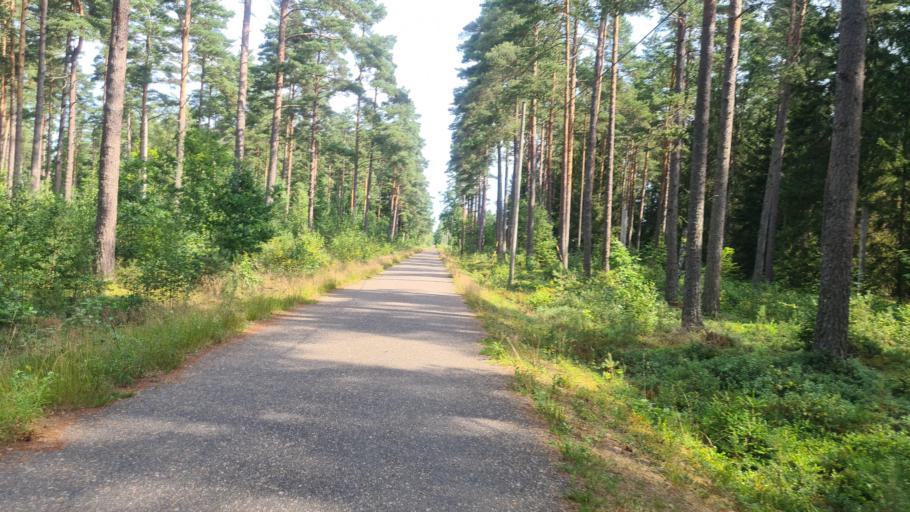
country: SE
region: Kronoberg
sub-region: Ljungby Kommun
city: Ljungby
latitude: 56.8451
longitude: 13.9634
